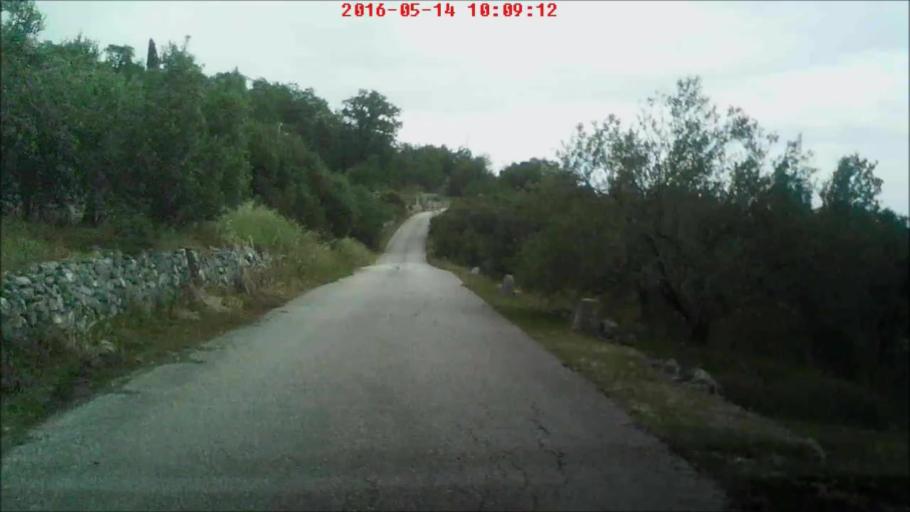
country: HR
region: Dubrovacko-Neretvanska
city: Podgora
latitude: 42.7455
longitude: 17.9374
